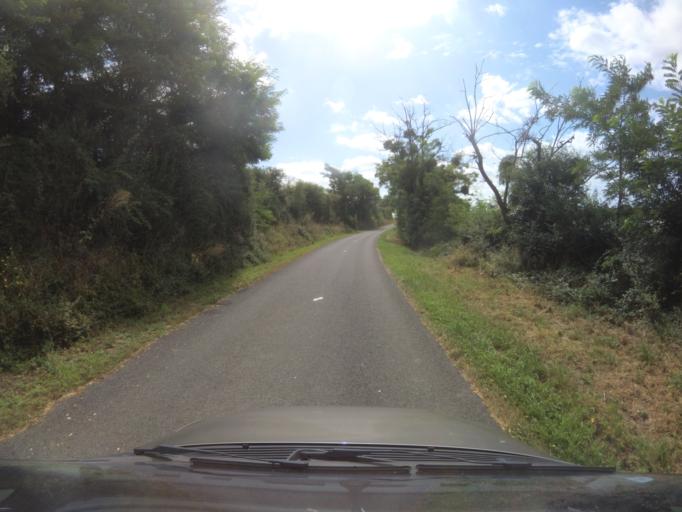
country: FR
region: Pays de la Loire
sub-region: Departement de Maine-et-Loire
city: Nueil-sur-Layon
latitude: 47.1795
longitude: -0.3491
